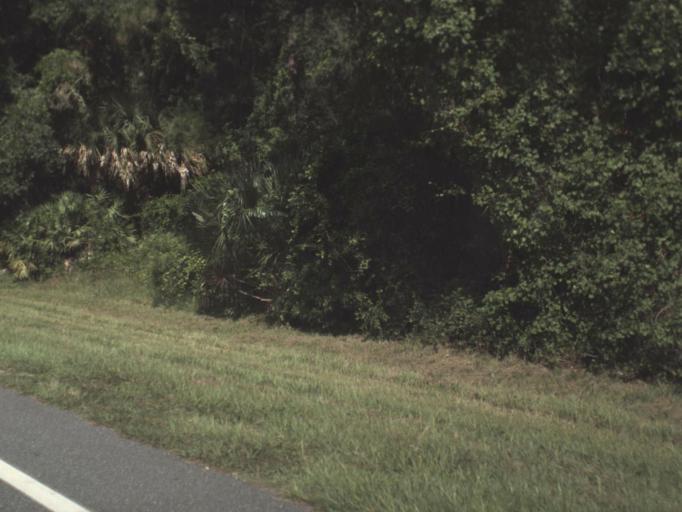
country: US
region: Florida
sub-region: Putnam County
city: Palatka
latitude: 29.5907
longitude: -81.6046
